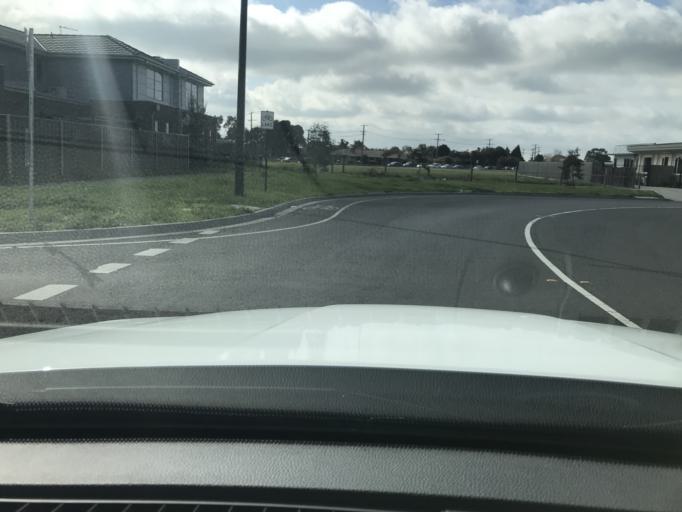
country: AU
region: Victoria
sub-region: Hume
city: Roxburgh Park
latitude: -37.5940
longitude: 144.9177
